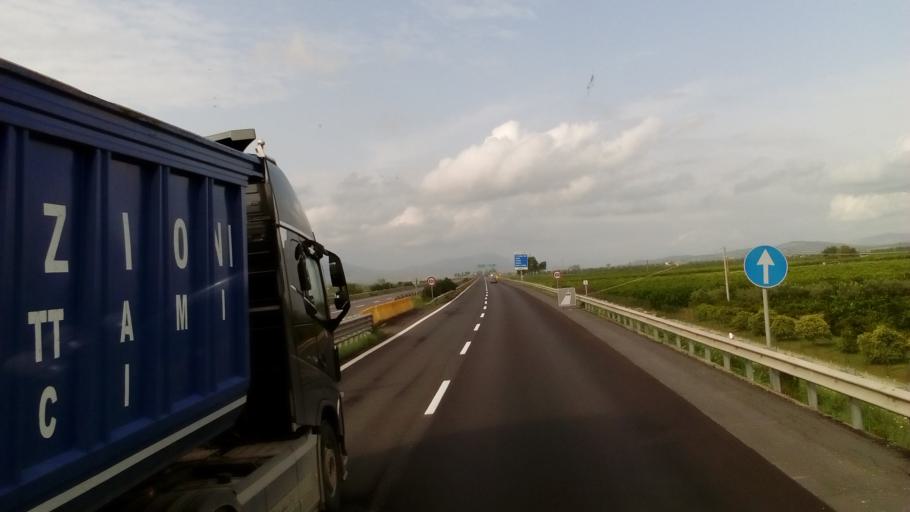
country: IT
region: Sicily
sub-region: Catania
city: Paterno
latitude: 37.4892
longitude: 14.8320
